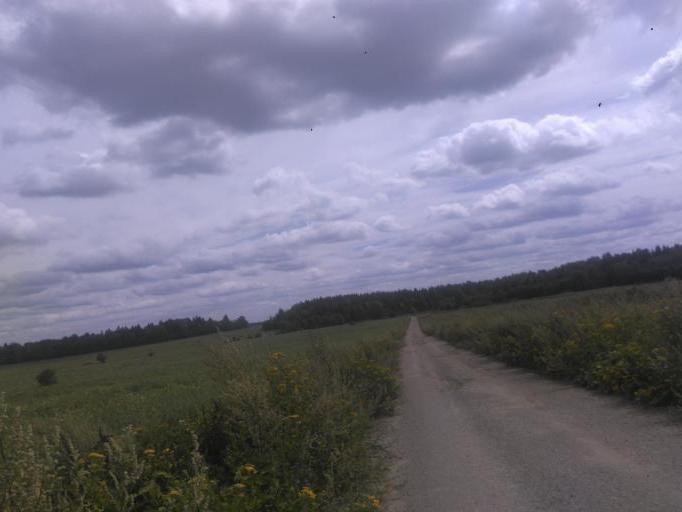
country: RU
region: Moskovskaya
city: Solnechnogorsk
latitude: 56.1436
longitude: 36.9237
